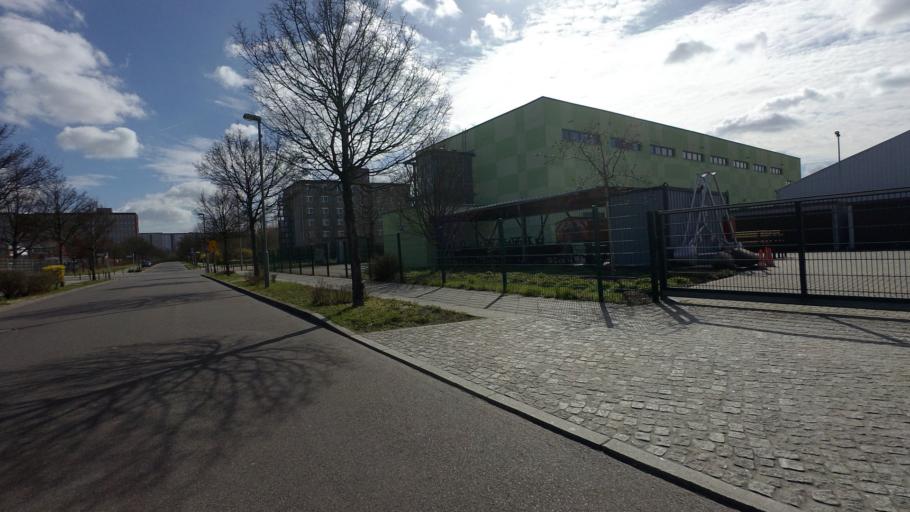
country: DE
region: Berlin
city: Falkenberg
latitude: 52.5582
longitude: 13.5480
